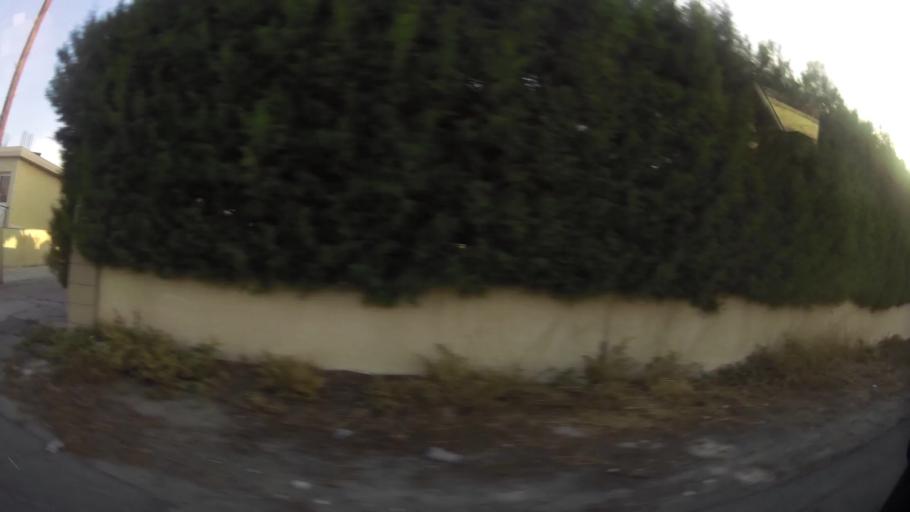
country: CY
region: Larnaka
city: Aradippou
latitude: 34.9233
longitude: 33.5926
